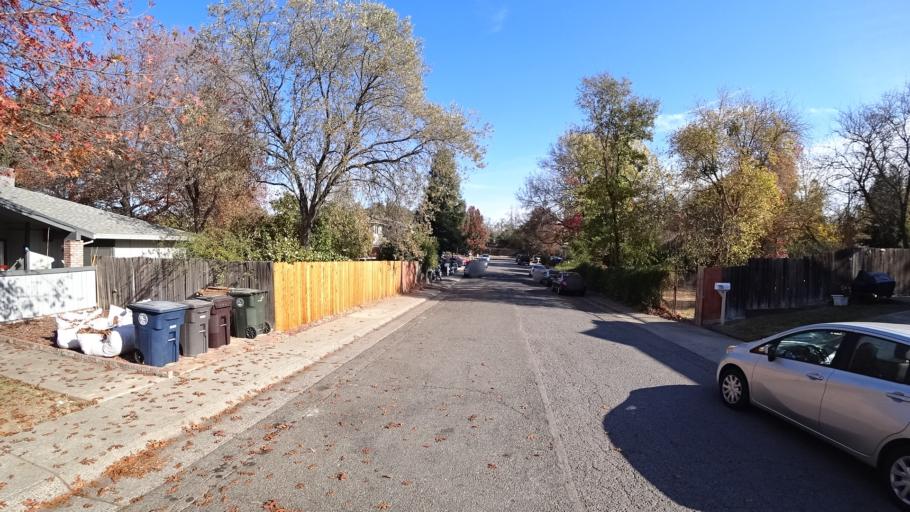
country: US
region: California
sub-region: Sacramento County
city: Fair Oaks
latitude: 38.6665
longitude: -121.2908
